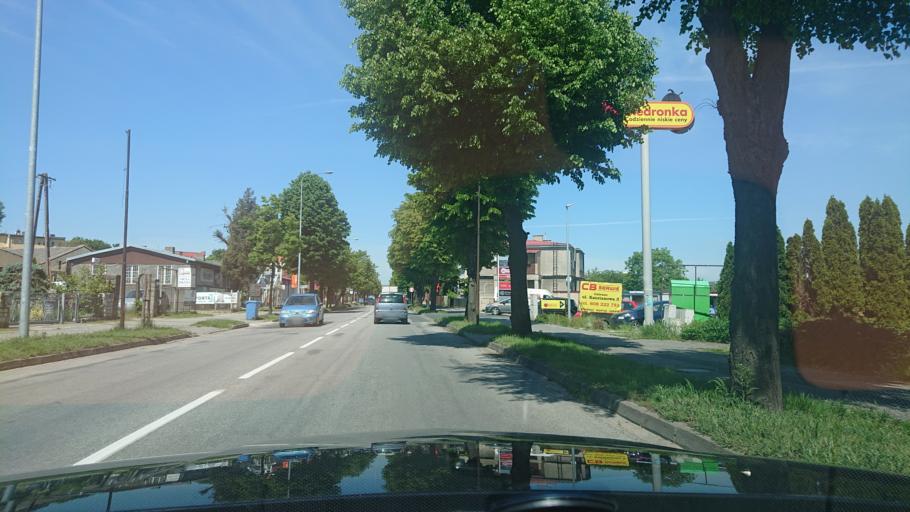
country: PL
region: Greater Poland Voivodeship
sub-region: Powiat gnieznienski
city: Gniezno
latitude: 52.5246
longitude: 17.6006
